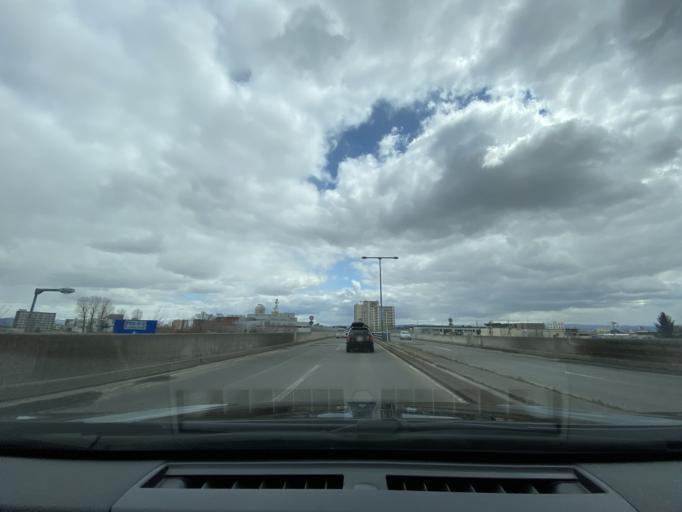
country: JP
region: Hokkaido
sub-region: Asahikawa-shi
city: Asahikawa
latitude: 43.7551
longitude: 142.3677
